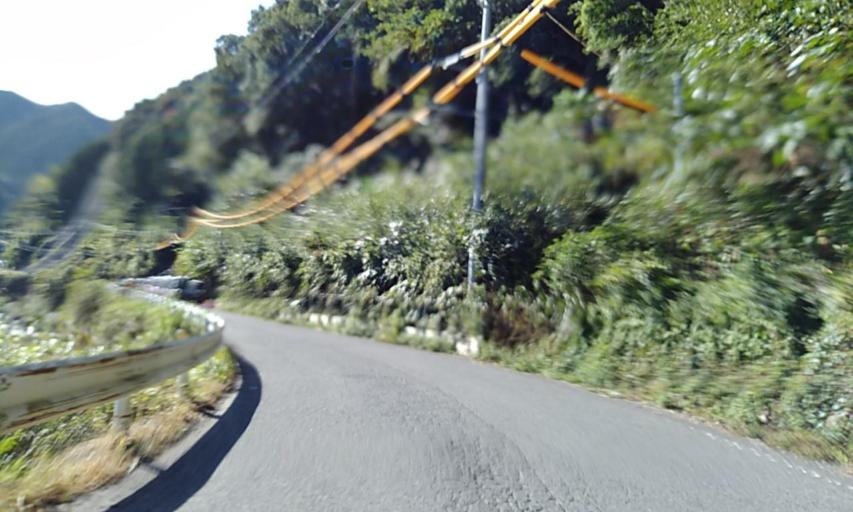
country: JP
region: Wakayama
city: Kainan
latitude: 34.0520
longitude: 135.3141
